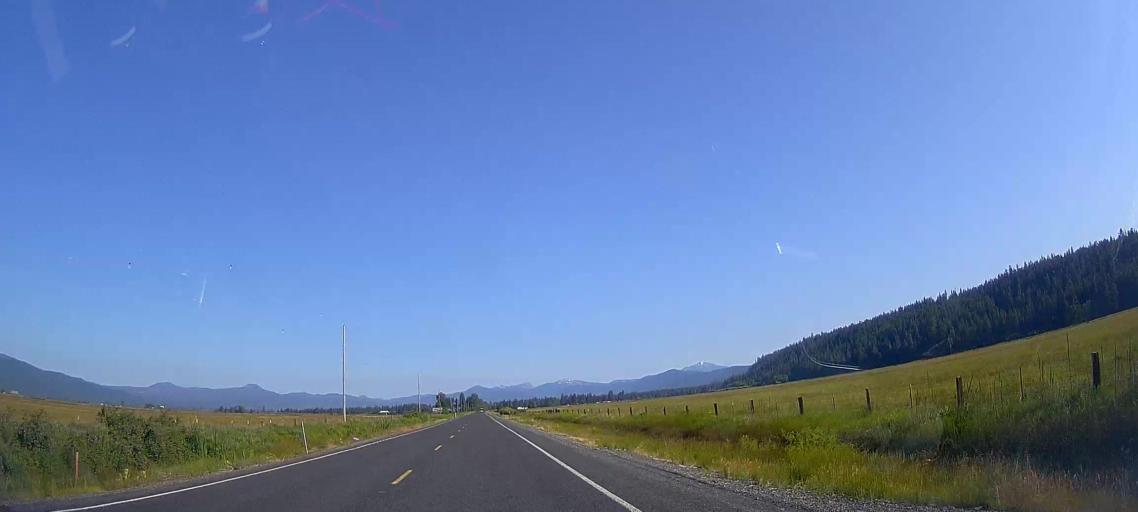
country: US
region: Oregon
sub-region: Klamath County
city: Klamath Falls
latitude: 42.6564
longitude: -121.9601
